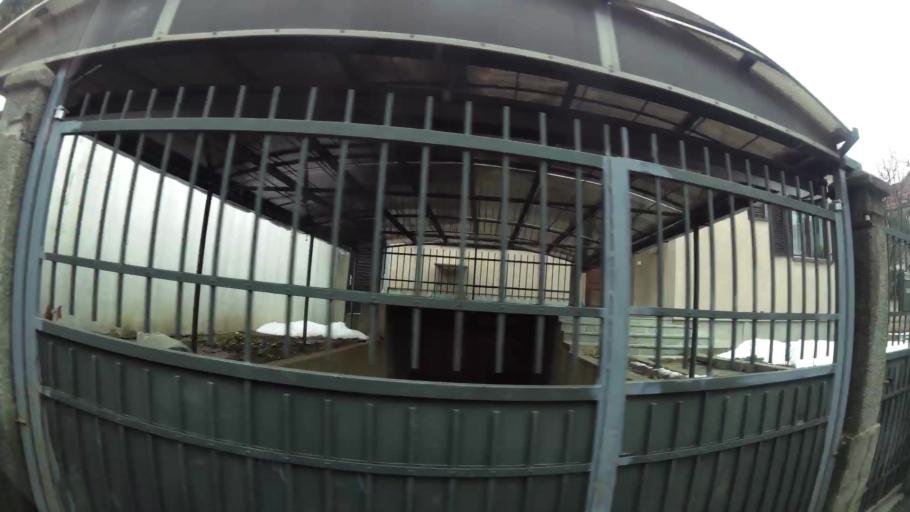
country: RS
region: Central Serbia
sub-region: Belgrade
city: Vozdovac
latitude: 44.7626
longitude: 20.5010
